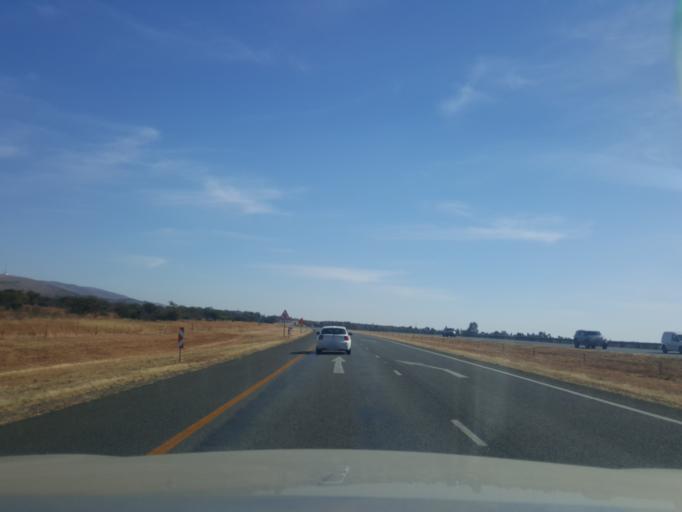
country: ZA
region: North-West
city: Ga-Rankuwa
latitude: -25.6556
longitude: 28.0370
